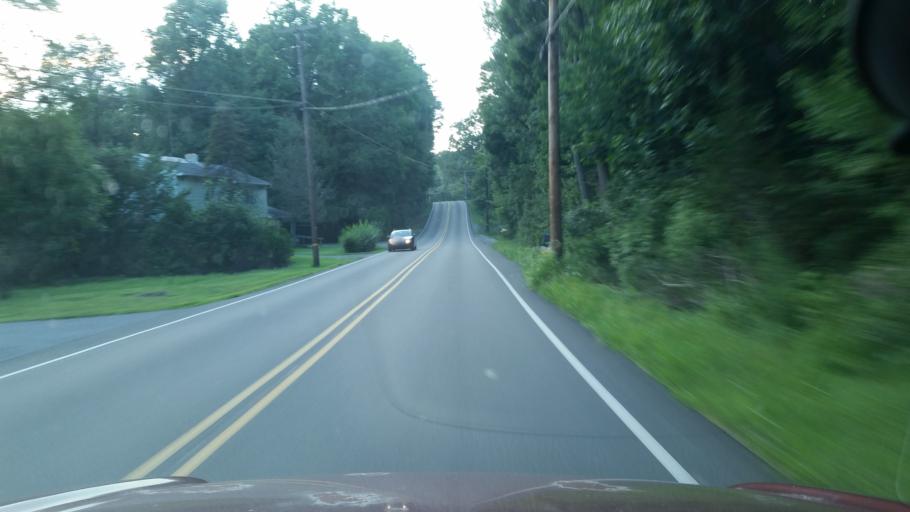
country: US
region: Pennsylvania
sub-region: Lebanon County
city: Campbelltown
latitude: 40.2489
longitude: -76.5400
